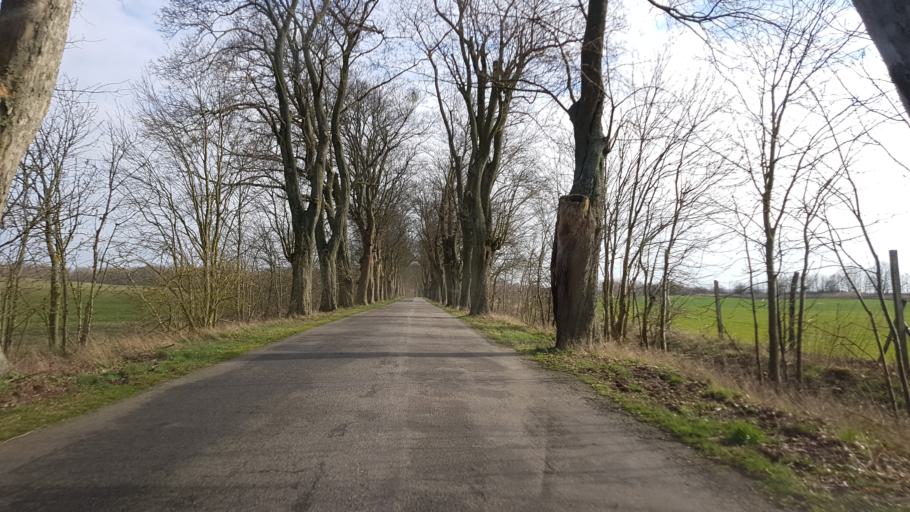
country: PL
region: West Pomeranian Voivodeship
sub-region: Powiat policki
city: Dobra
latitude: 53.5422
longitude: 14.3116
